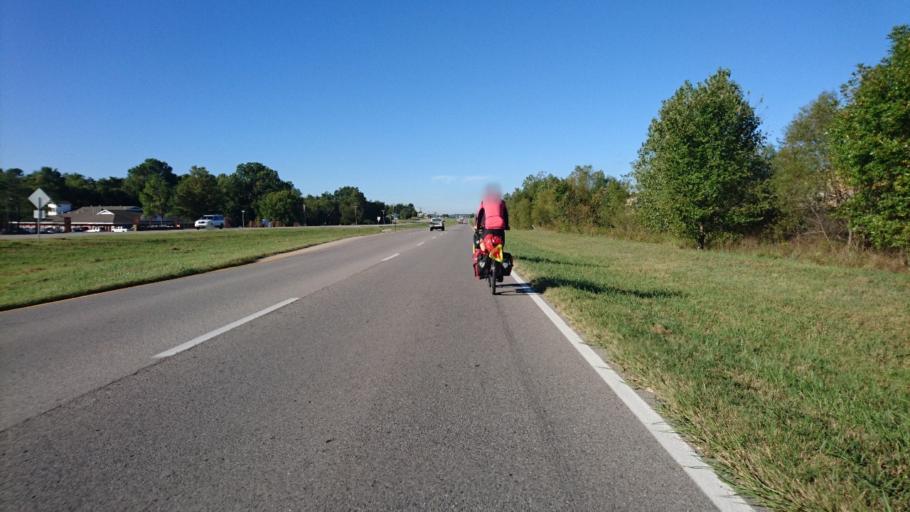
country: US
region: Oklahoma
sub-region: Rogers County
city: Verdigris
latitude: 36.2402
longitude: -95.6806
